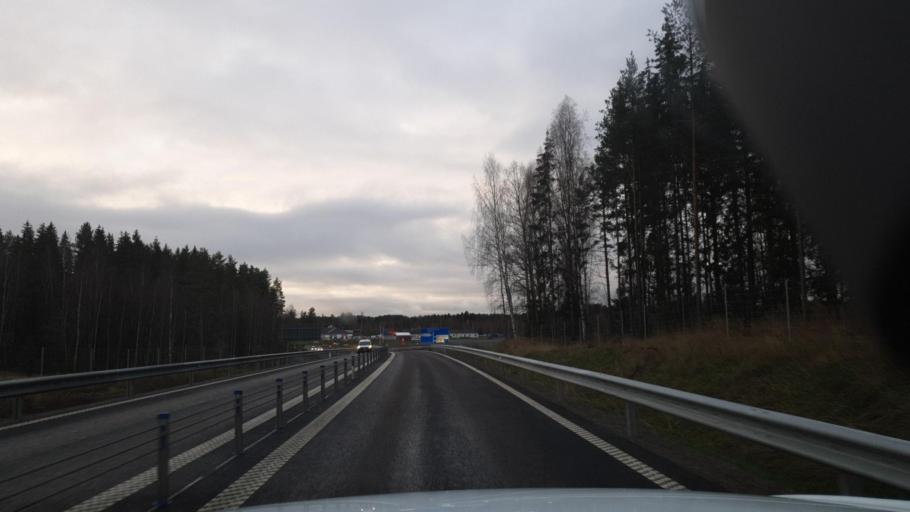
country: SE
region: Vaermland
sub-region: Arvika Kommun
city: Arvika
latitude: 59.6817
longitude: 12.5935
